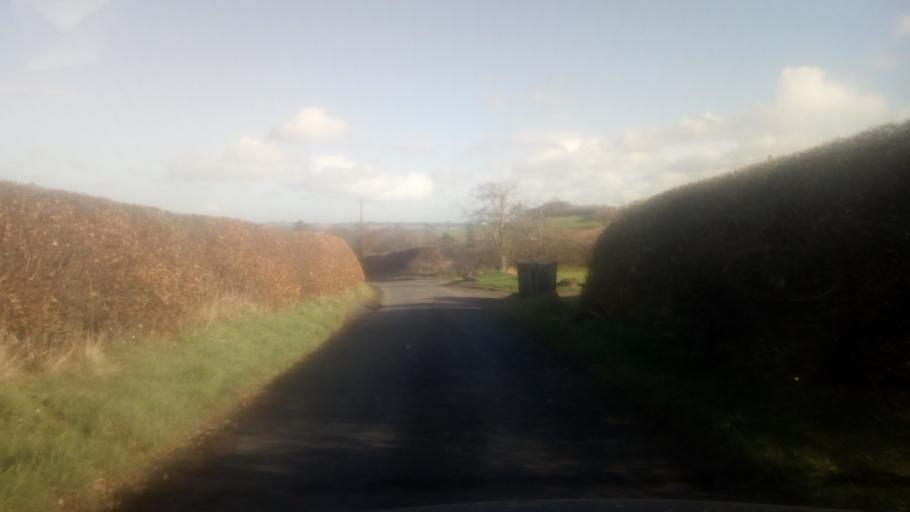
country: GB
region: Scotland
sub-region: The Scottish Borders
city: Jedburgh
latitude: 55.5035
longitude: -2.5044
